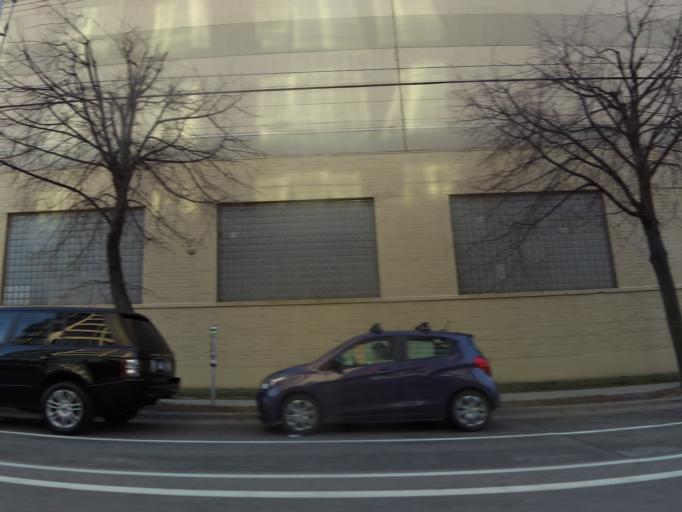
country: US
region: Minnesota
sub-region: Hennepin County
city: Minneapolis
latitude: 44.9753
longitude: -93.2500
